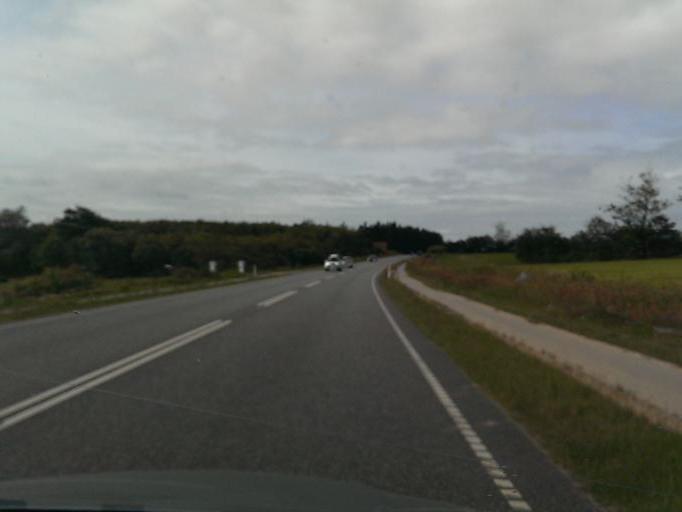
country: DK
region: North Denmark
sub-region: Hjorring Kommune
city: Hjorring
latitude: 57.4474
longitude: 9.9105
